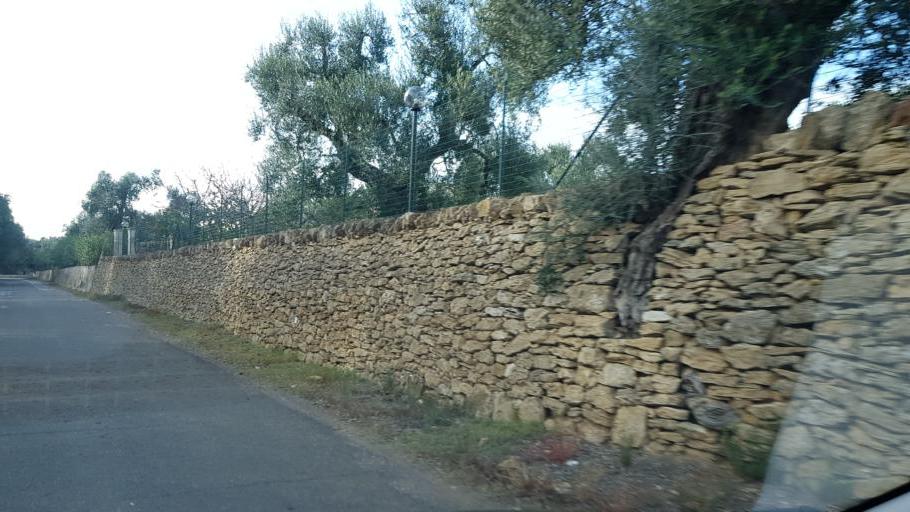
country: IT
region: Apulia
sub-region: Provincia di Brindisi
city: Oria
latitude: 40.5098
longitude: 17.6697
